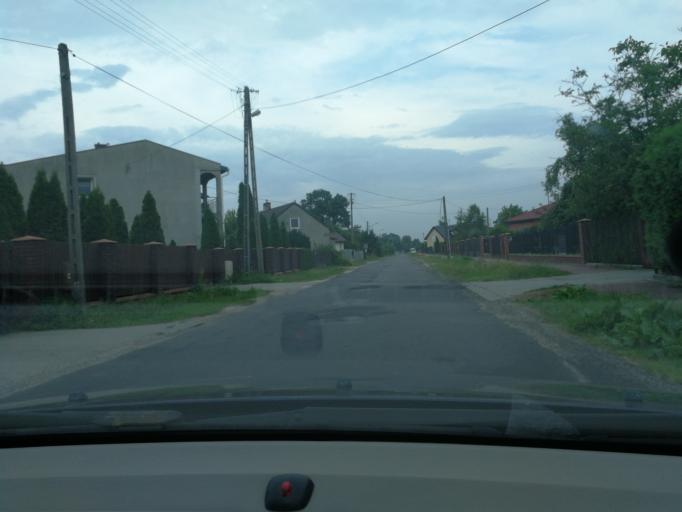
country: PL
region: Masovian Voivodeship
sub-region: Powiat grodziski
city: Grodzisk Mazowiecki
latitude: 52.1283
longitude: 20.6050
